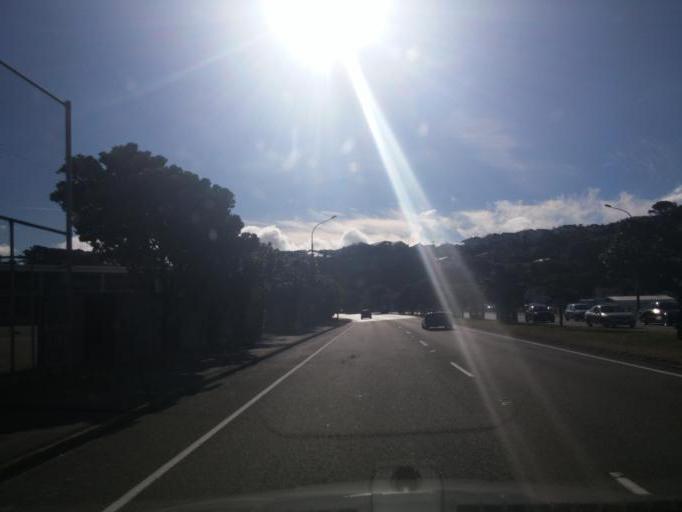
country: NZ
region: Wellington
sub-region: Wellington City
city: Wellington
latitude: -41.3135
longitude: 174.7981
